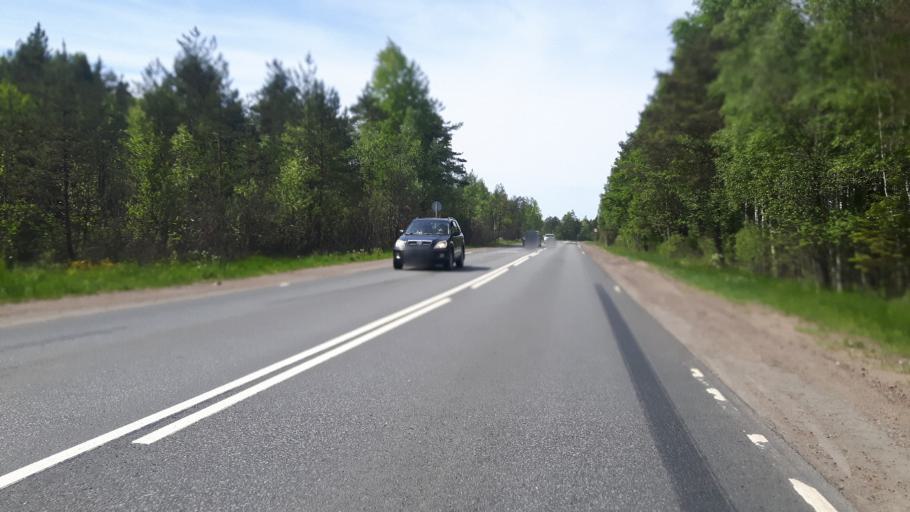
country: RU
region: Leningrad
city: Ust'-Luga
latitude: 59.6600
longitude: 28.4114
